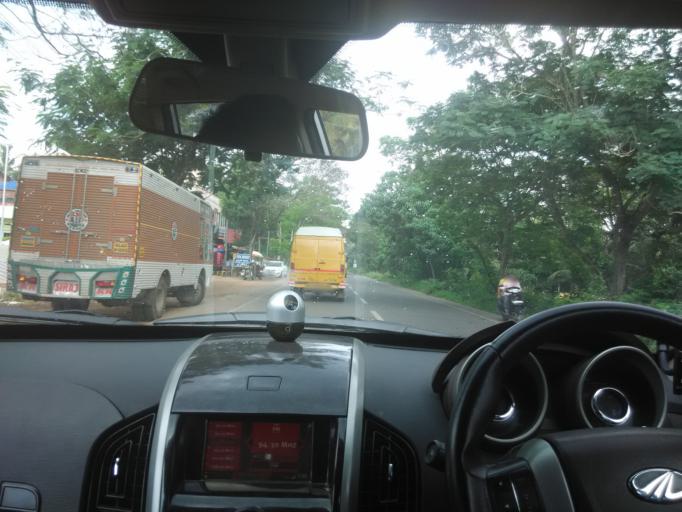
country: IN
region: Kerala
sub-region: Thiruvananthapuram
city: Attingal
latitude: 8.6438
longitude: 76.8433
